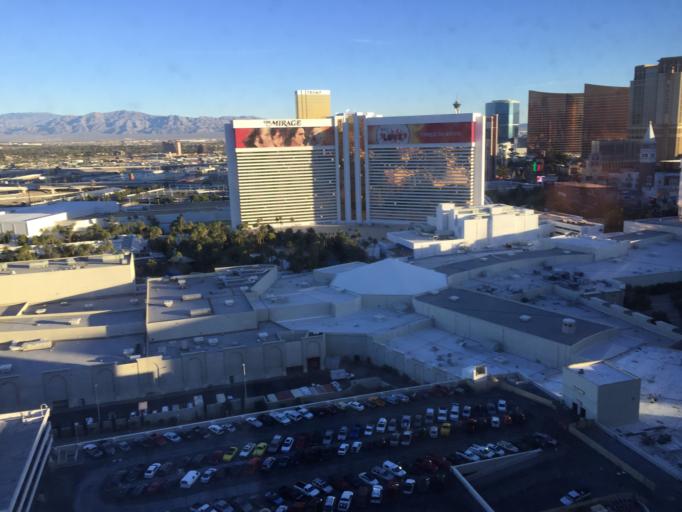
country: US
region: Nevada
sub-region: Clark County
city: Paradise
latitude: 36.1172
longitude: -115.1772
